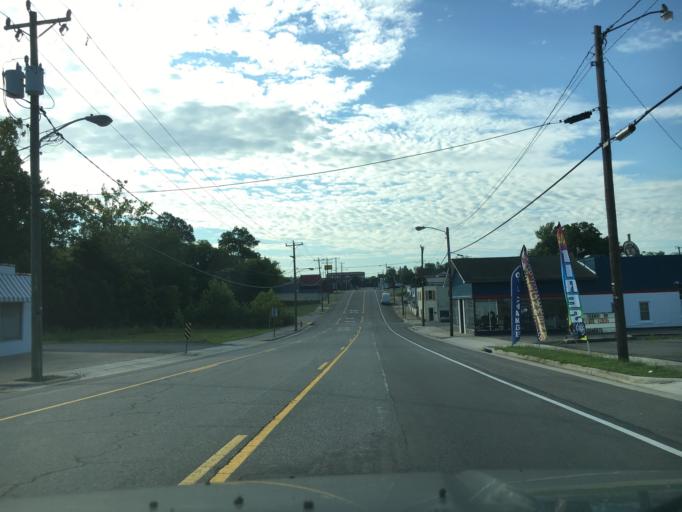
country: US
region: Virginia
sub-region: Halifax County
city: South Boston
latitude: 36.7022
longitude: -78.9059
